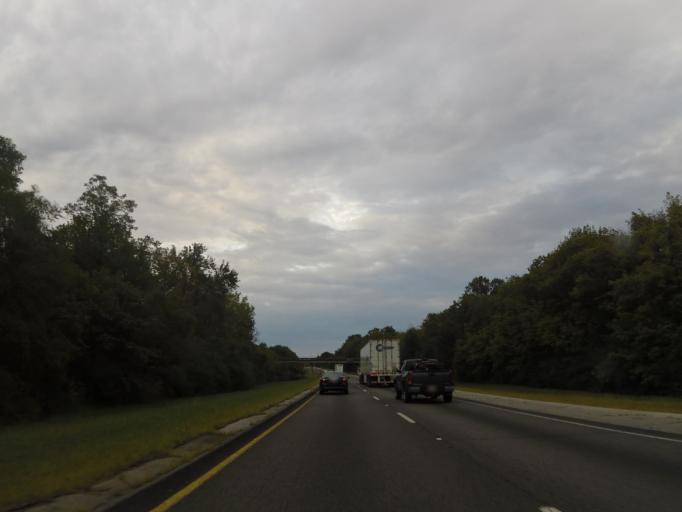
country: US
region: Alabama
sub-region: Jefferson County
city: Argo
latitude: 33.6689
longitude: -86.5530
